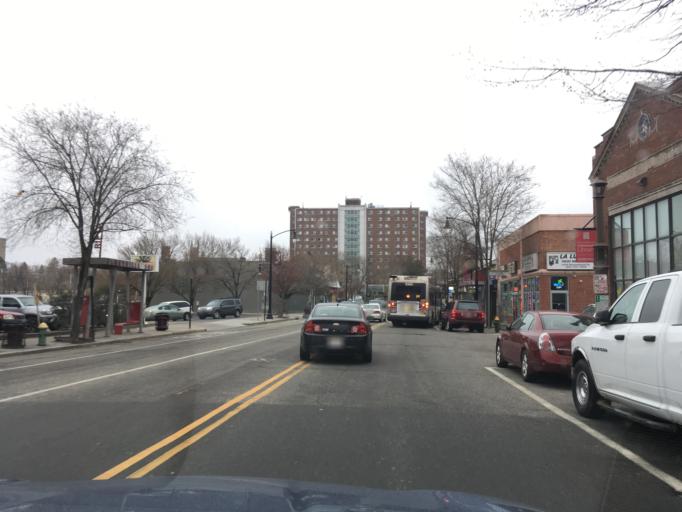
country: US
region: Rhode Island
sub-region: Providence County
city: Providence
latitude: 41.8167
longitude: -71.4432
